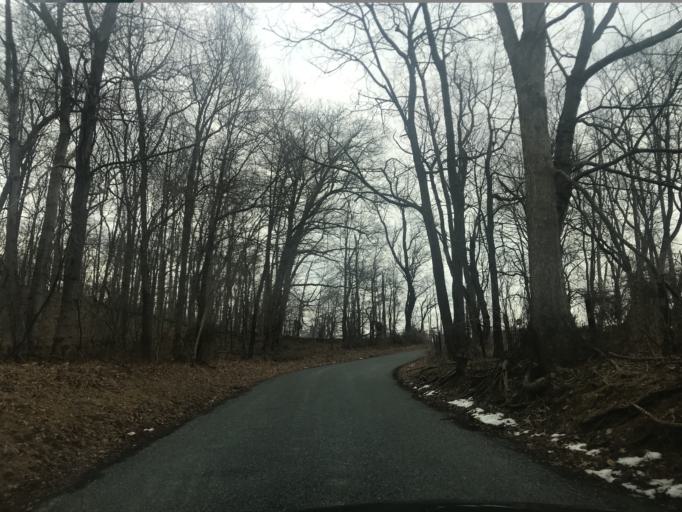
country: US
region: Maryland
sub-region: Harford County
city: Jarrettsville
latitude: 39.6729
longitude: -76.4112
